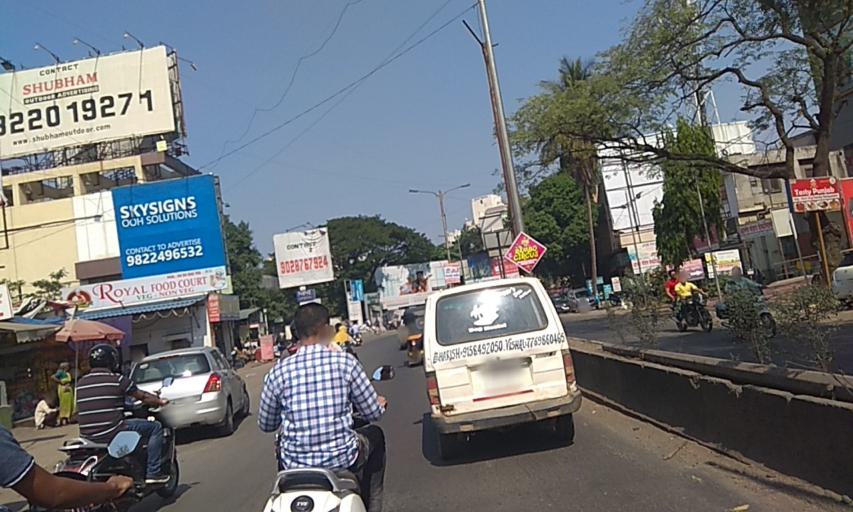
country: IN
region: Maharashtra
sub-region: Pune Division
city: Pune
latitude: 18.5055
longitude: 73.9277
